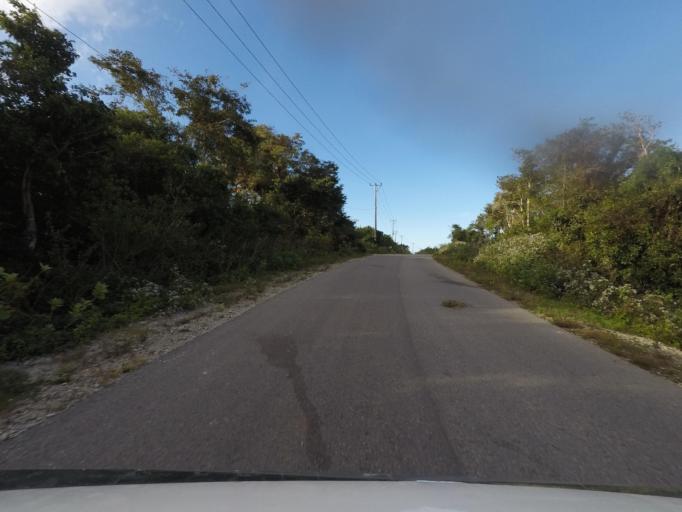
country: TL
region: Lautem
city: Lospalos
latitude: -8.4033
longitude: 127.0015
